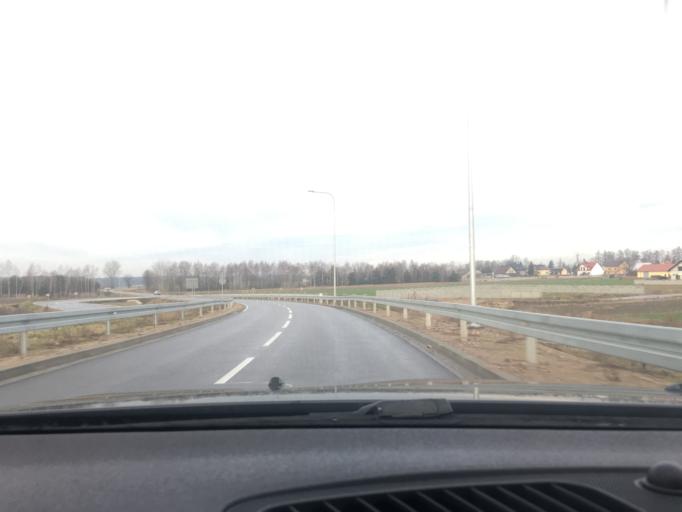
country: PL
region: Swietokrzyskie
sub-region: Powiat jedrzejowski
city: Sobkow
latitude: 50.6919
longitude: 20.3687
